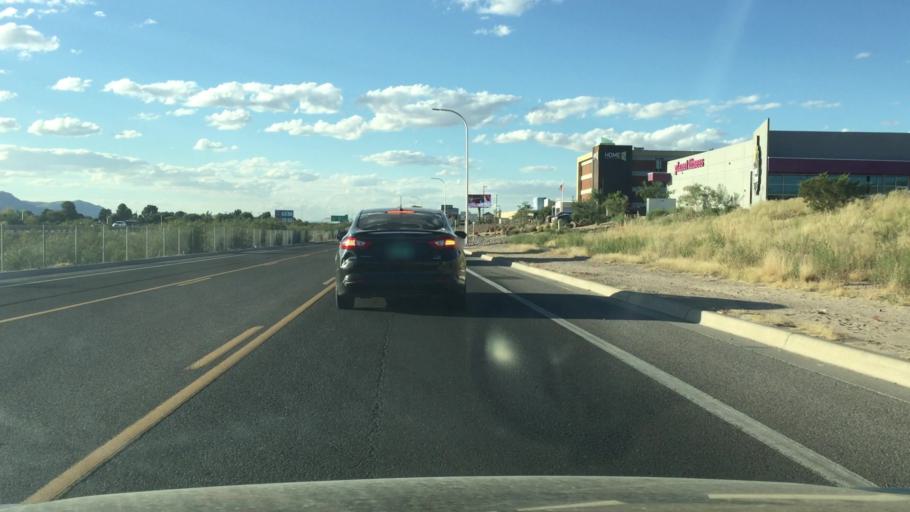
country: US
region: New Mexico
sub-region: Dona Ana County
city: Las Cruces
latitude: 32.3345
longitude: -106.7596
